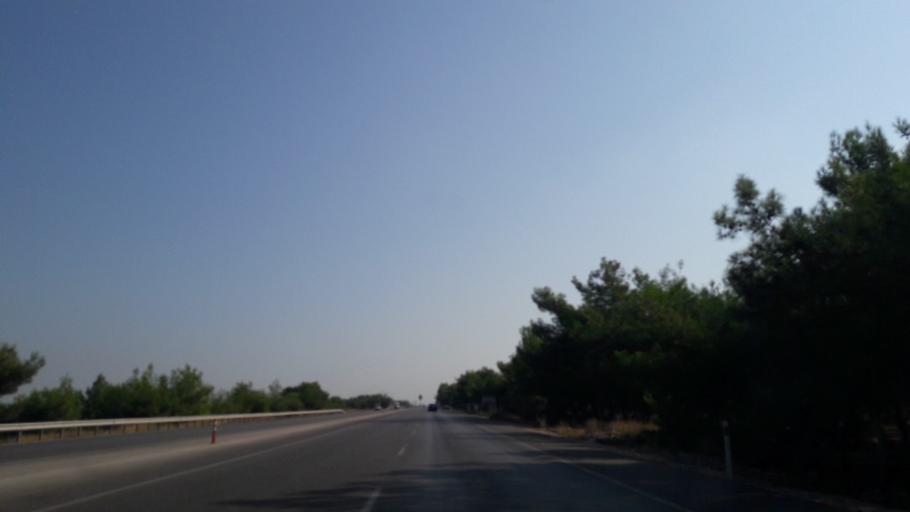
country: TR
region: Adana
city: Yuregir
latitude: 37.0868
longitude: 35.4862
